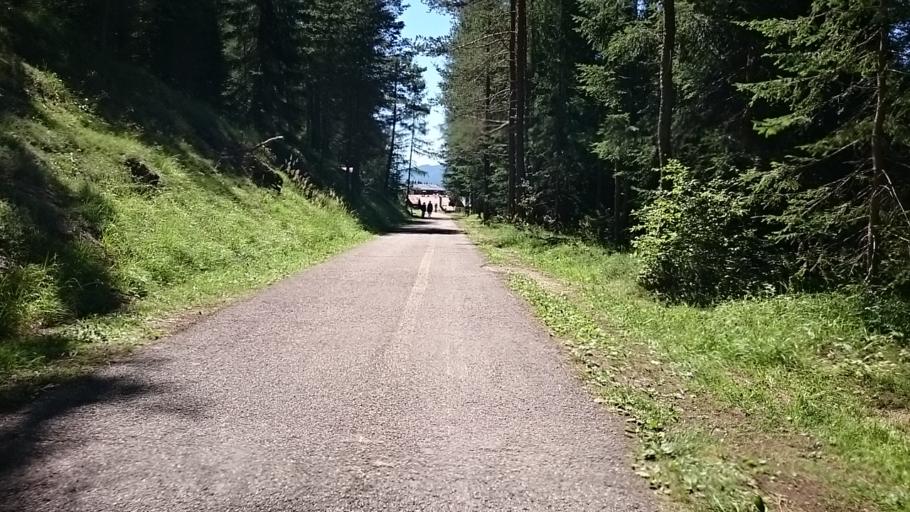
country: IT
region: Veneto
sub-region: Provincia di Belluno
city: Cortina d'Ampezzo
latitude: 46.5569
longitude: 12.1280
